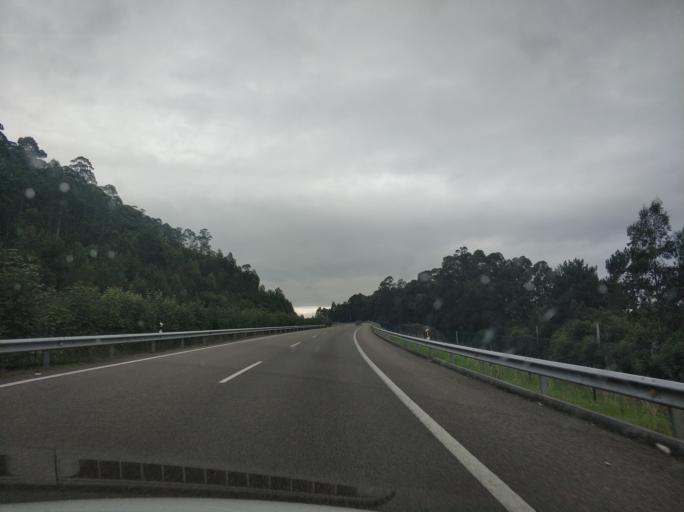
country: ES
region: Galicia
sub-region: Provincia de Lugo
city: Ribadeo
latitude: 43.5350
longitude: -7.1244
